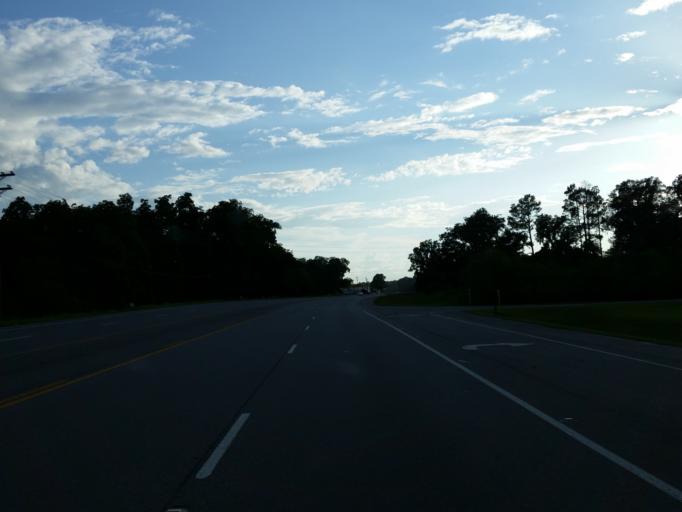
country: US
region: Georgia
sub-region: Clinch County
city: Homerville
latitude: 31.0318
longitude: -82.7674
